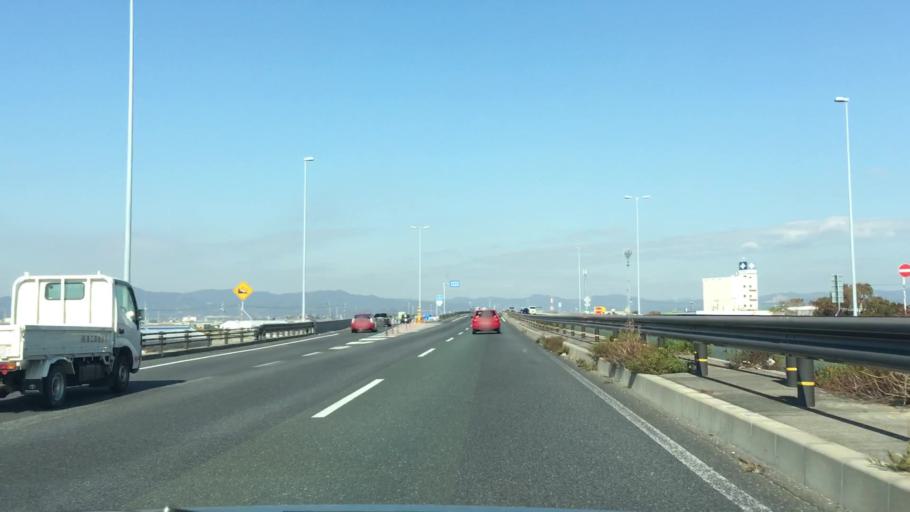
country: JP
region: Aichi
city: Kozakai-cho
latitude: 34.7584
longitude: 137.3335
